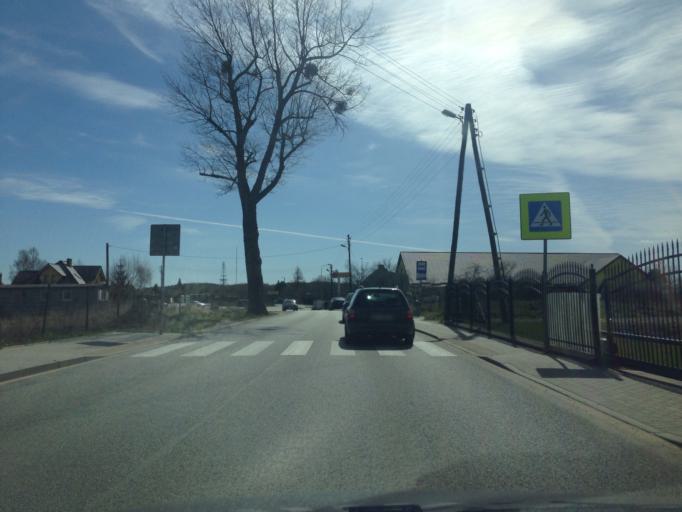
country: PL
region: Pomeranian Voivodeship
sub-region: Powiat kartuski
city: Chwaszczyno
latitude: 54.4835
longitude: 18.4373
